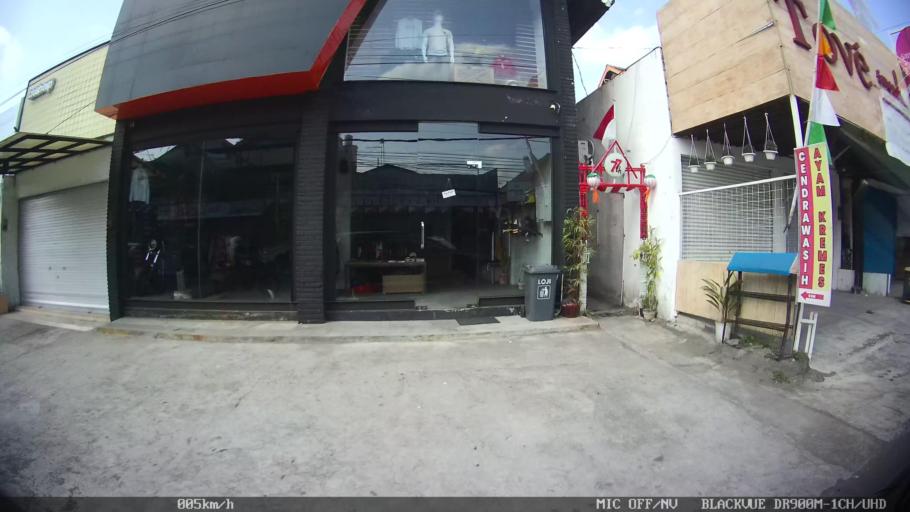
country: ID
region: Daerah Istimewa Yogyakarta
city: Yogyakarta
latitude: -7.7797
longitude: 110.3900
